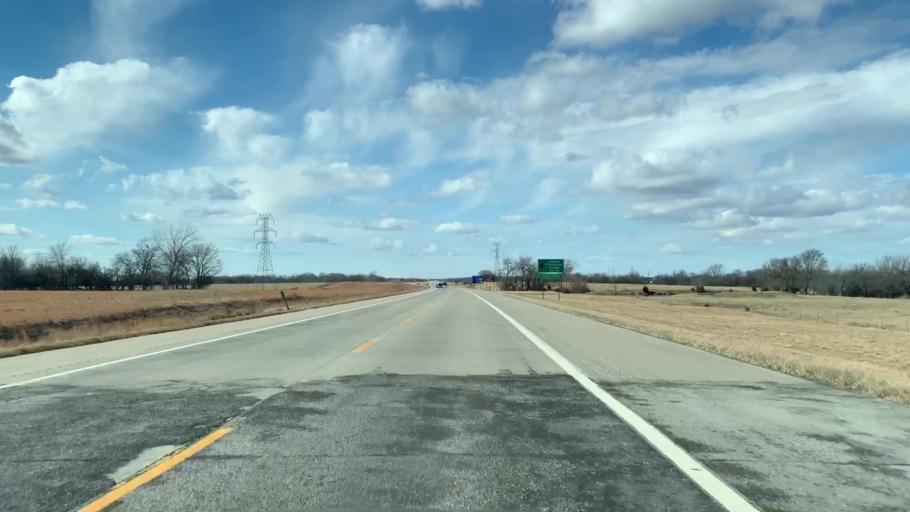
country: US
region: Kansas
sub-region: Labette County
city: Parsons
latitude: 37.3634
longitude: -95.2373
